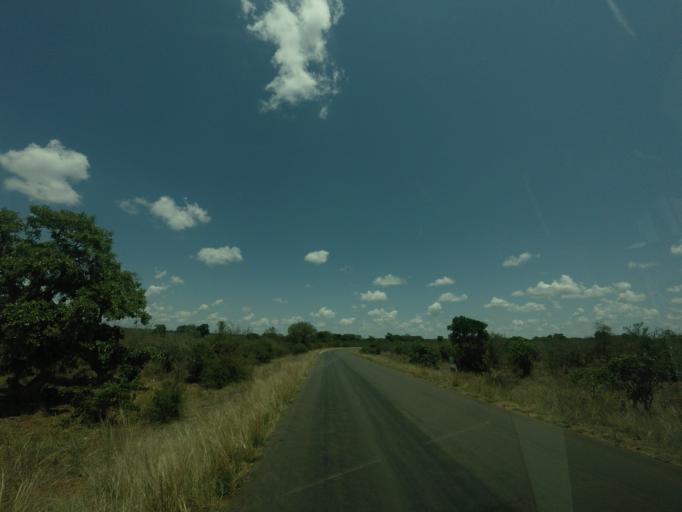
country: ZA
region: Mpumalanga
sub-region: Ehlanzeni District
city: Komatipoort
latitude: -24.7896
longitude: 31.8615
